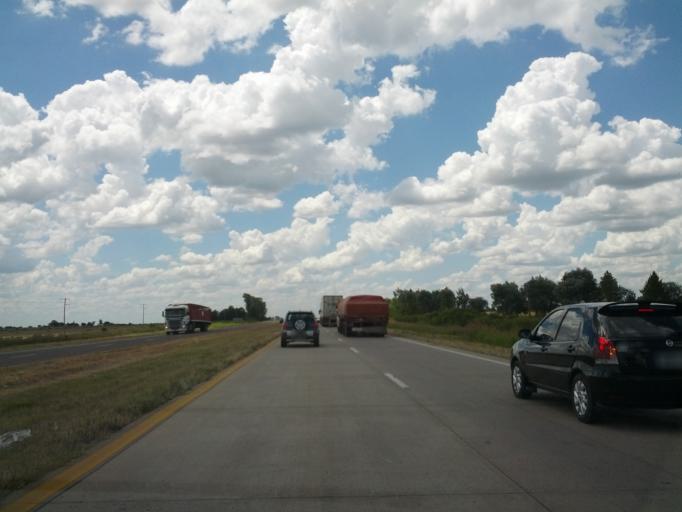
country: AR
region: Entre Rios
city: Gualeguaychu
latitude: -33.0020
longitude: -58.6025
